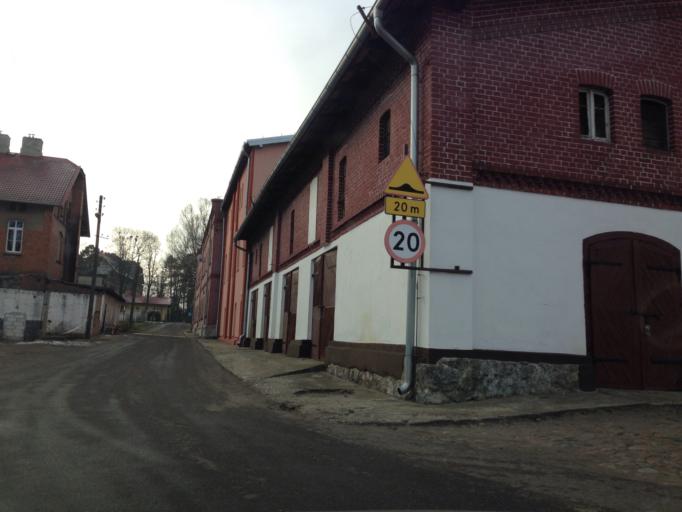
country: PL
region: Warmian-Masurian Voivodeship
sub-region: Powiat ketrzynski
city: Ketrzyn
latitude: 54.0759
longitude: 21.4229
